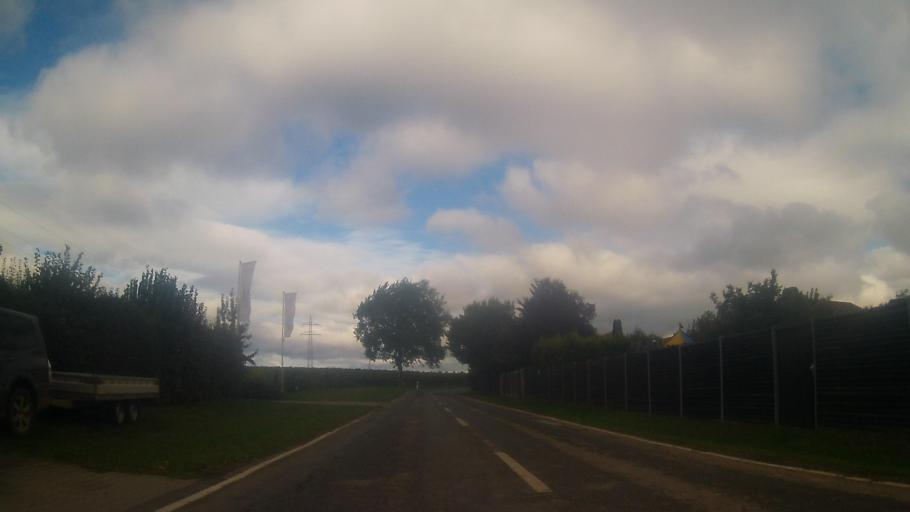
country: DE
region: Rheinland-Pfalz
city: Sulzheim
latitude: 49.8337
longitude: 8.1082
